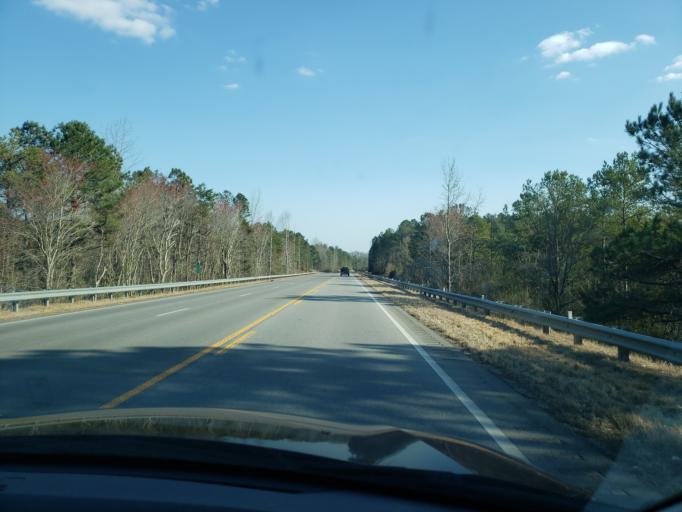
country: US
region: Alabama
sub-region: Randolph County
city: Wedowee
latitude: 33.4407
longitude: -85.5635
